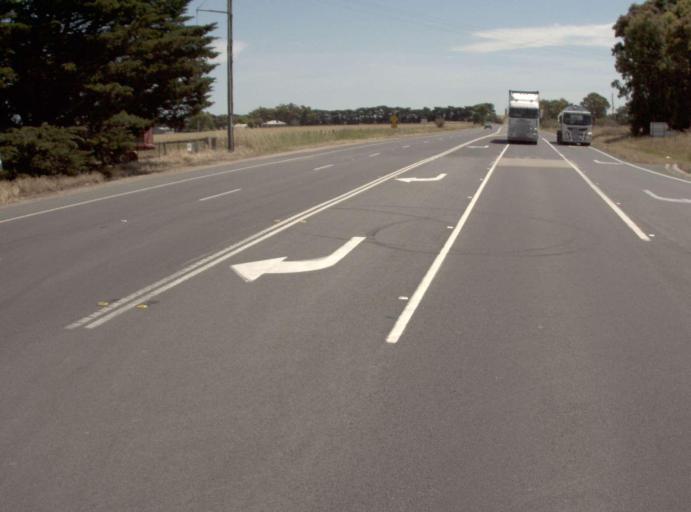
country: AU
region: Victoria
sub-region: Wellington
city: Heyfield
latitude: -38.1192
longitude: 146.8605
